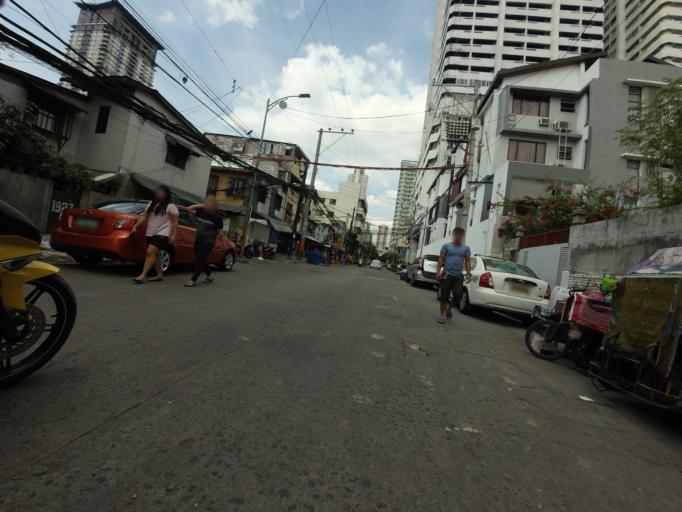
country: PH
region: Metro Manila
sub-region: City of Manila
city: Port Area
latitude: 14.5703
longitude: 120.9880
